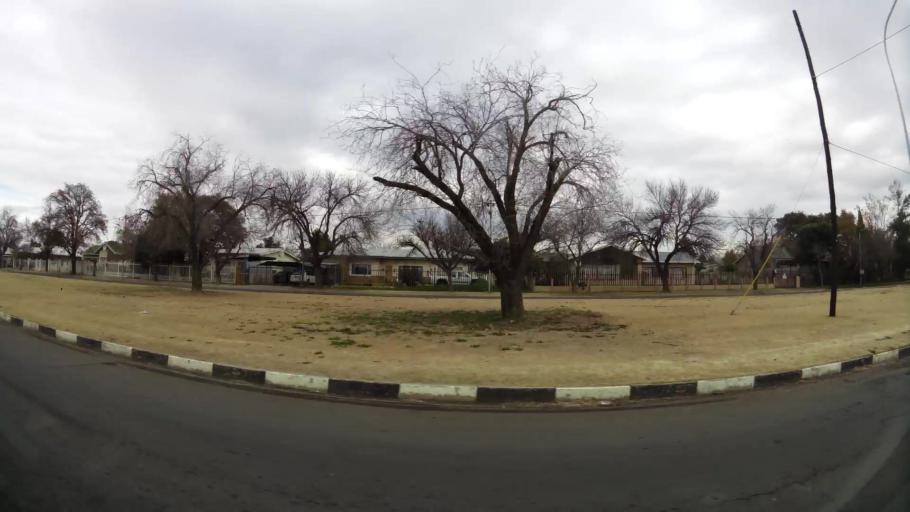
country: ZA
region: Orange Free State
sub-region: Fezile Dabi District Municipality
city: Kroonstad
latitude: -27.6327
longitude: 27.2332
